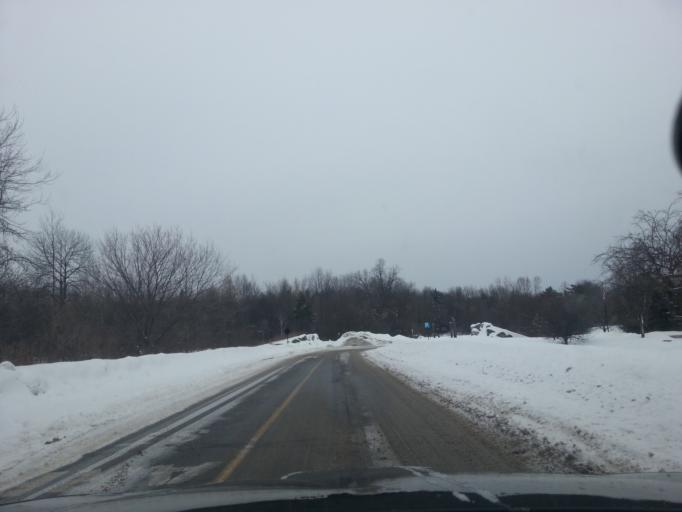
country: CA
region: Ontario
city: Ottawa
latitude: 45.4394
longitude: -75.7619
